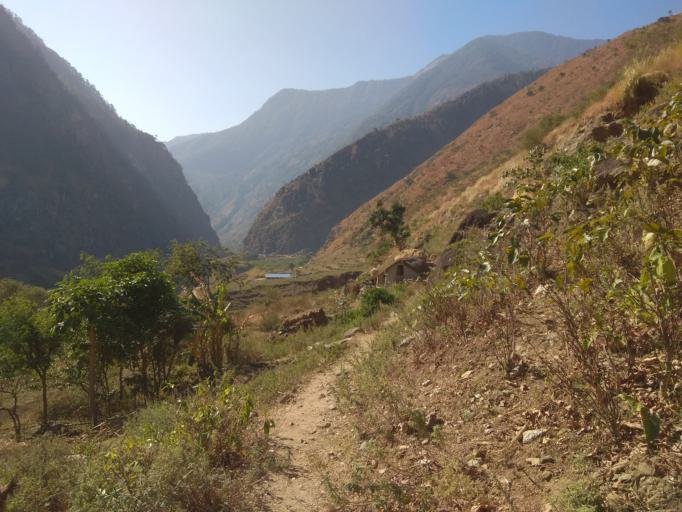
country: NP
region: Far Western
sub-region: Seti Zone
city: Achham
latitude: 29.2227
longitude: 81.6421
